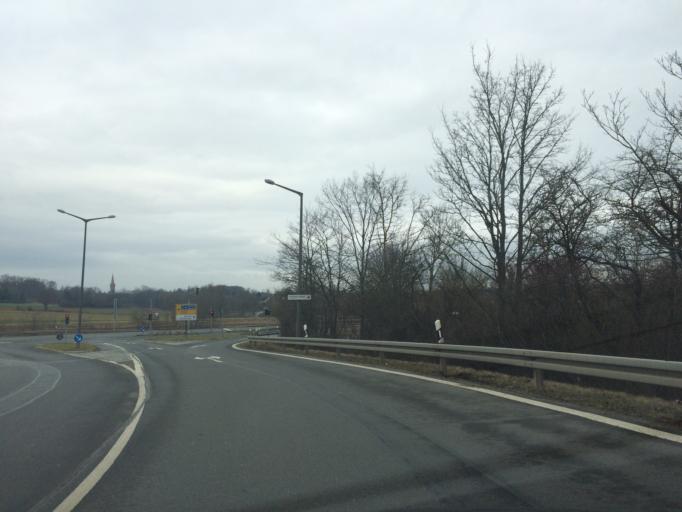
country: DE
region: Bavaria
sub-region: Regierungsbezirk Mittelfranken
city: Zirndorf
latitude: 49.4856
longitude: 10.9441
